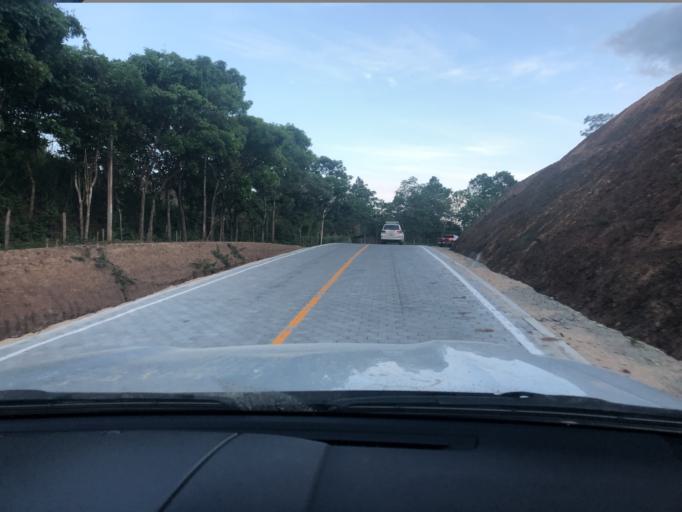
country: NI
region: Nueva Segovia
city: Ocotal
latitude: 13.6716
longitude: -86.6136
